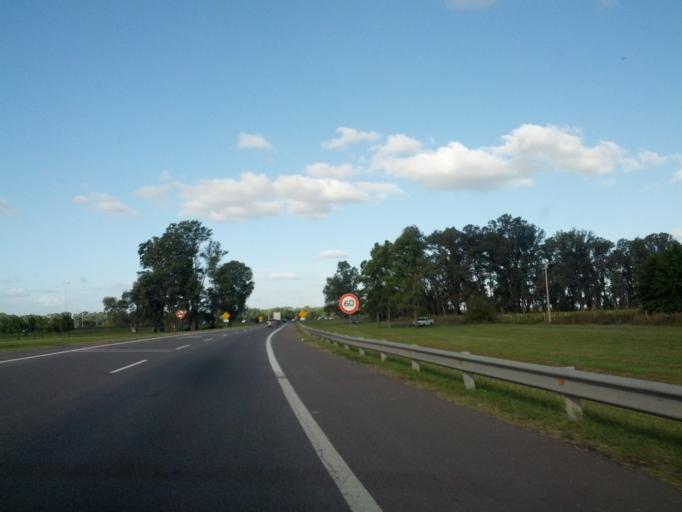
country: AR
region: Buenos Aires
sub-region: Partido de Lujan
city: Lujan
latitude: -34.5695
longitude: -59.0638
